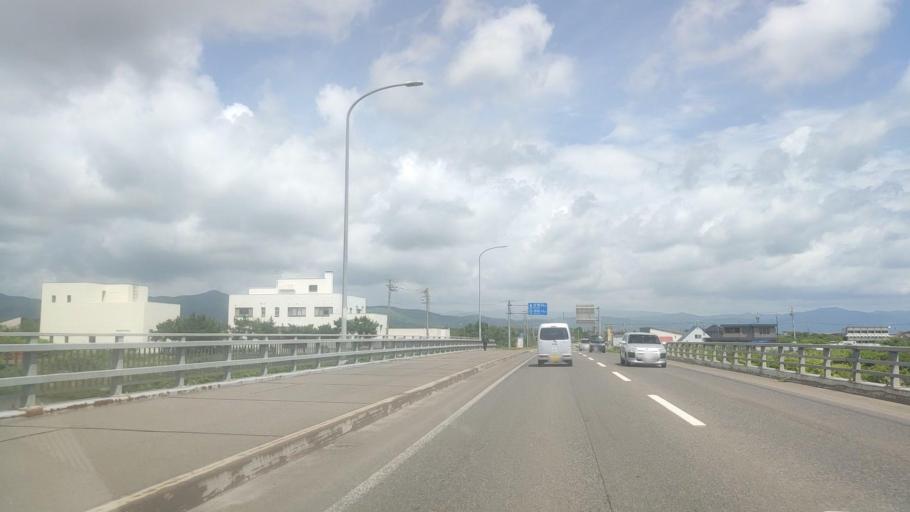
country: JP
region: Hokkaido
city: Niseko Town
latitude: 42.5189
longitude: 140.3820
